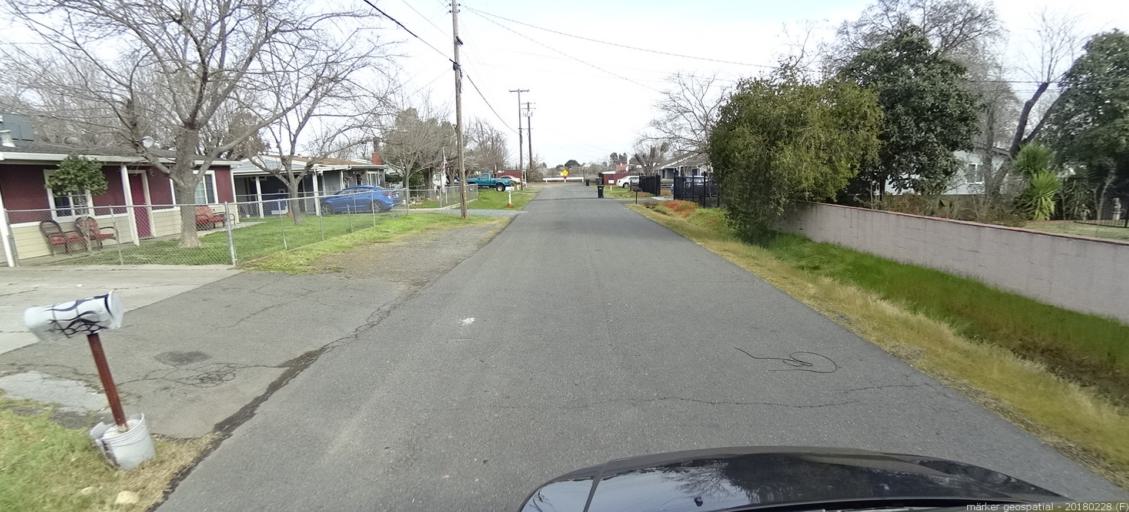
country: US
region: California
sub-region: Sacramento County
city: Rio Linda
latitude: 38.6993
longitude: -121.4487
